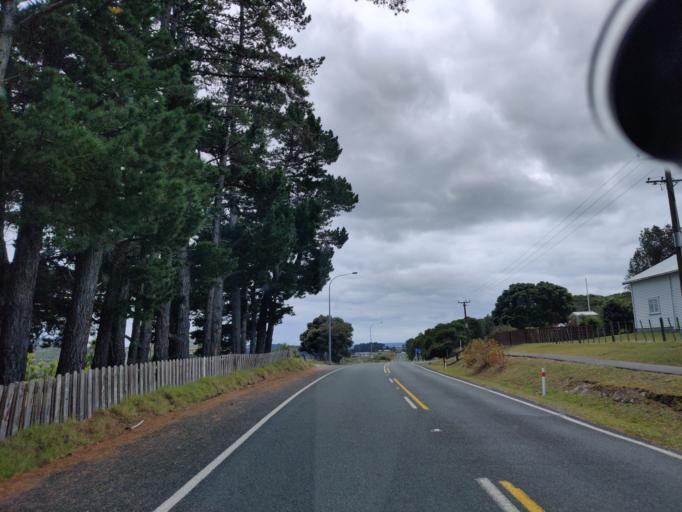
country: NZ
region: Northland
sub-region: Far North District
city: Kaitaia
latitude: -34.6505
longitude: 172.9703
